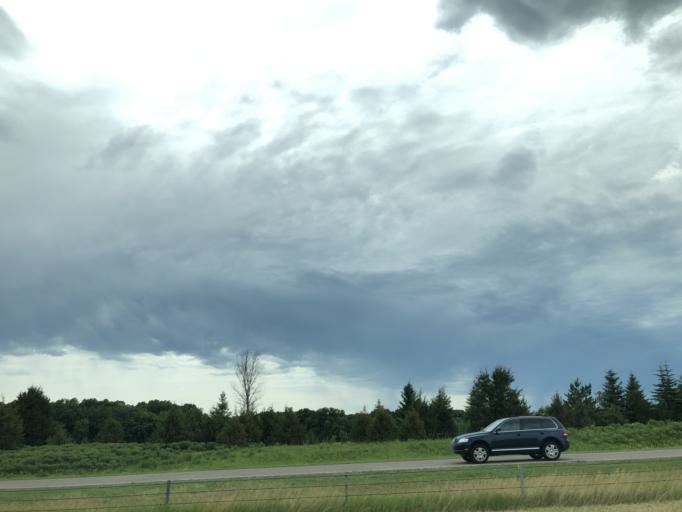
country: US
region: Minnesota
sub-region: Wright County
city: Clearwater
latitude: 45.3791
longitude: -94.0018
